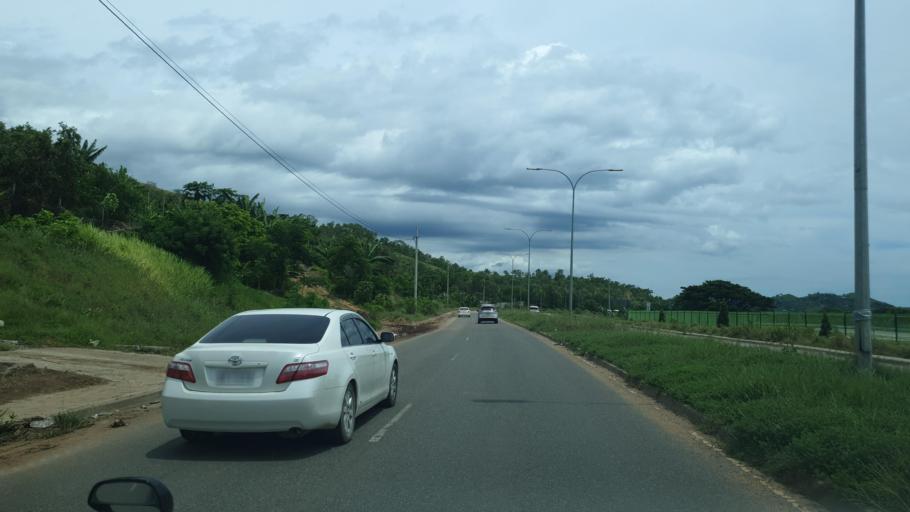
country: PG
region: National Capital
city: Port Moresby
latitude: -9.4956
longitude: 147.2268
